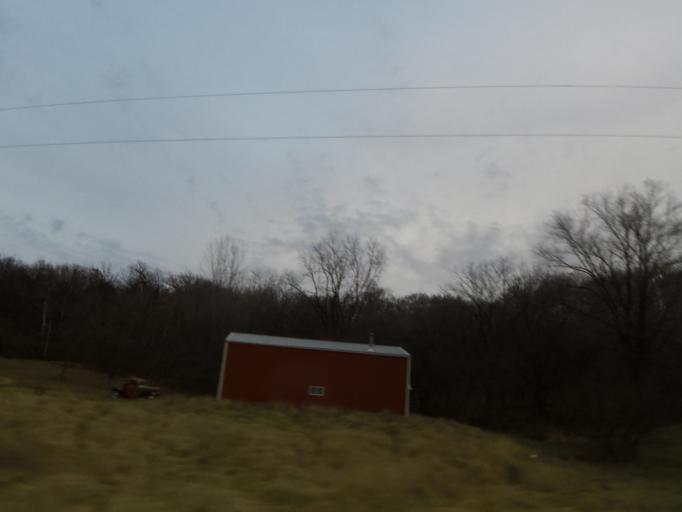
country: US
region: Wisconsin
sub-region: Pierce County
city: River Falls
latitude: 44.8813
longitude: -92.6009
